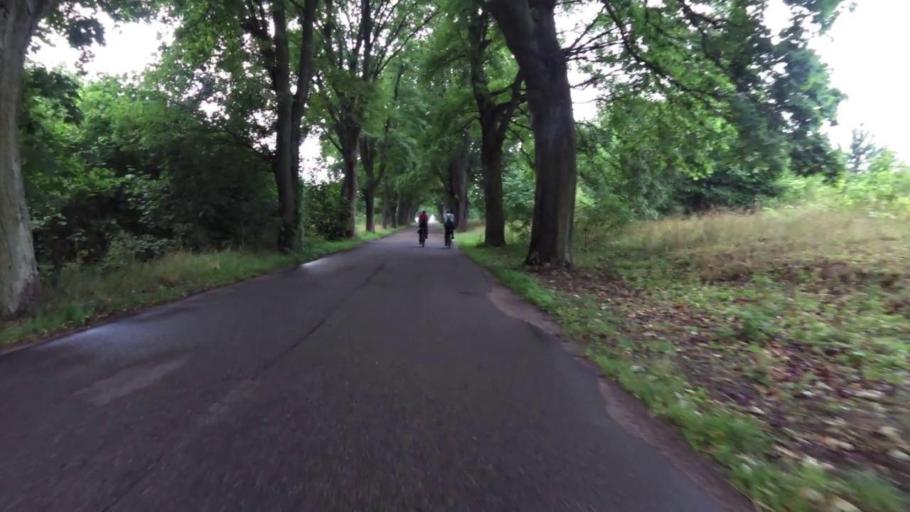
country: PL
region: West Pomeranian Voivodeship
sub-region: Powiat szczecinecki
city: Lubowo
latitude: 53.5877
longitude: 16.3802
